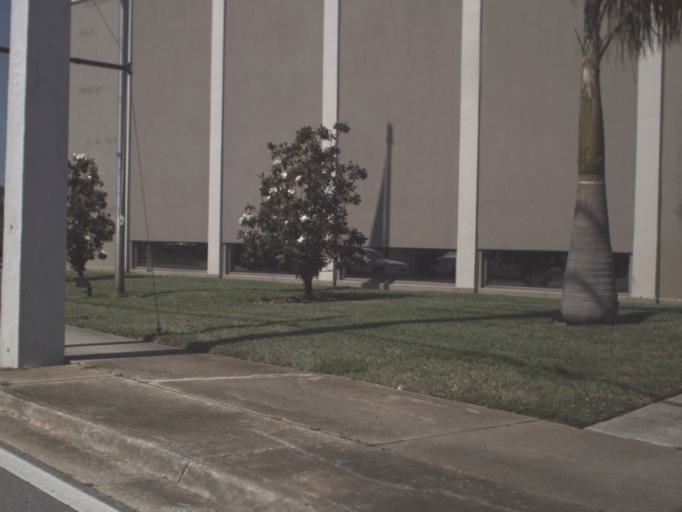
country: US
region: Florida
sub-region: Brevard County
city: Indian Harbour Beach
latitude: 28.1298
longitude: -80.6303
